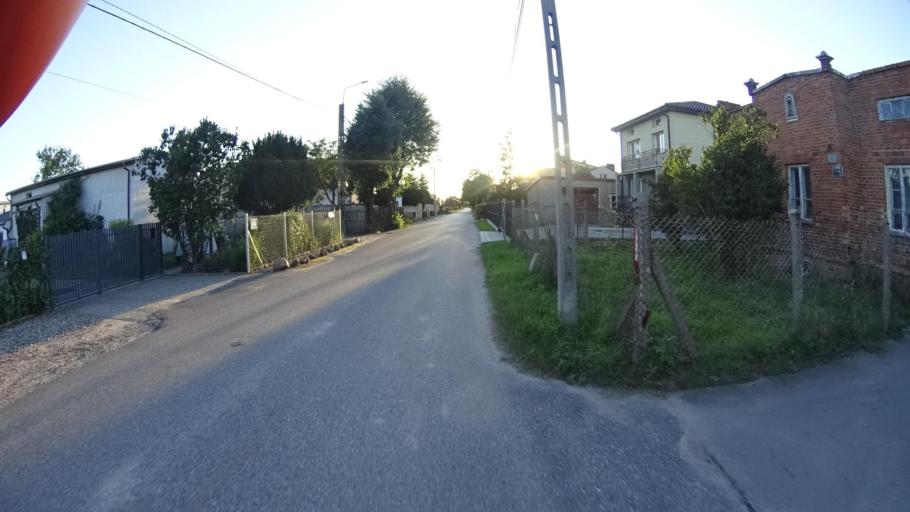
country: PL
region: Masovian Voivodeship
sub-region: Powiat warszawski zachodni
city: Ozarow Mazowiecki
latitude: 52.2244
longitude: 20.8207
